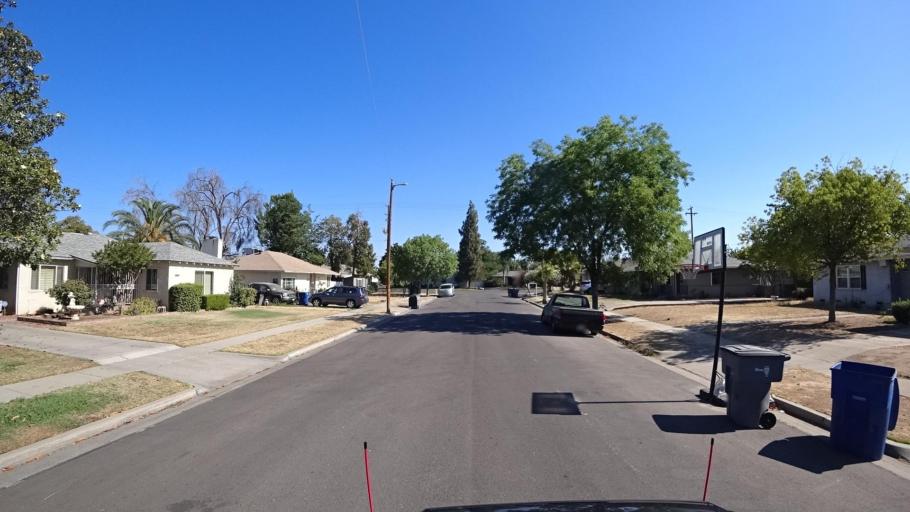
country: US
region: California
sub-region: Fresno County
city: Fresno
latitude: 36.7640
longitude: -119.8231
